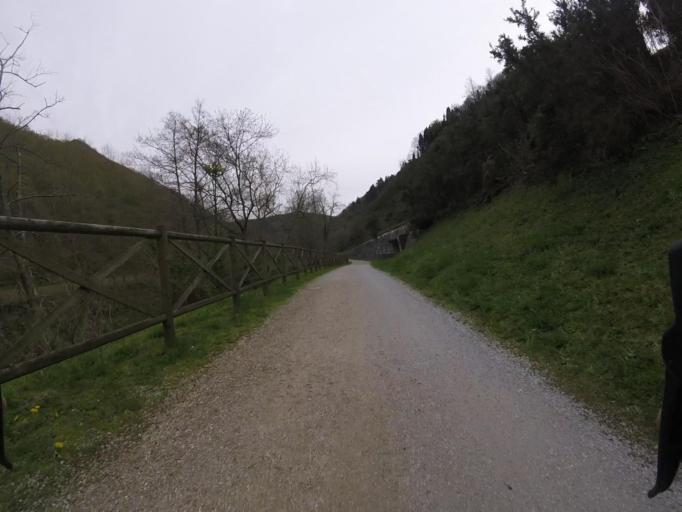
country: ES
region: Navarre
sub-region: Provincia de Navarra
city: Bera
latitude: 43.3037
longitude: -1.7341
